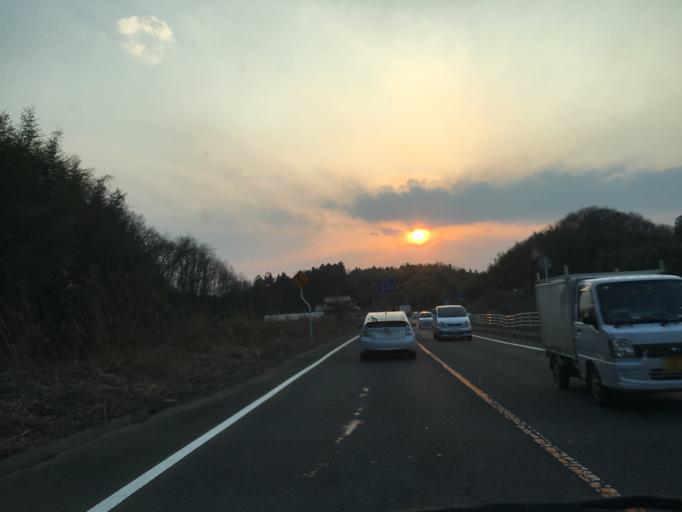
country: JP
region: Fukushima
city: Miharu
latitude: 37.4354
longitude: 140.4427
